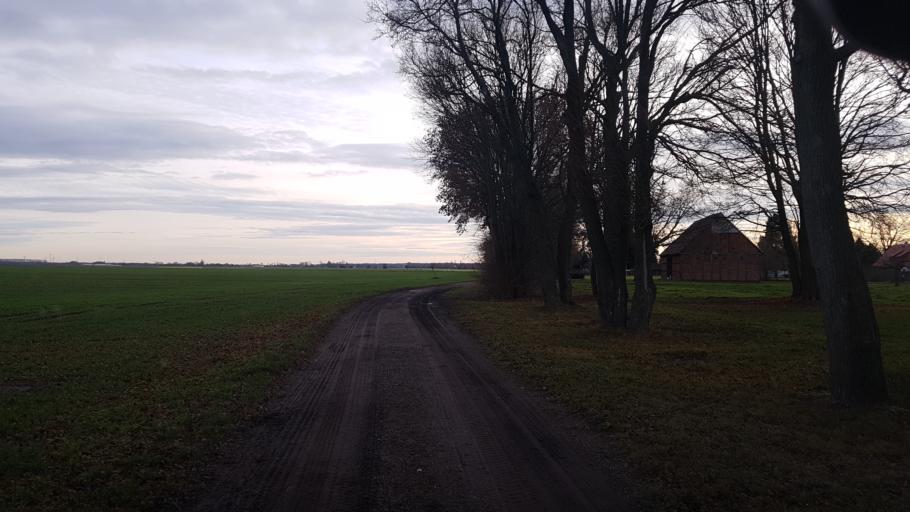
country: DE
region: Brandenburg
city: Doberlug-Kirchhain
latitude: 51.6756
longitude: 13.5117
